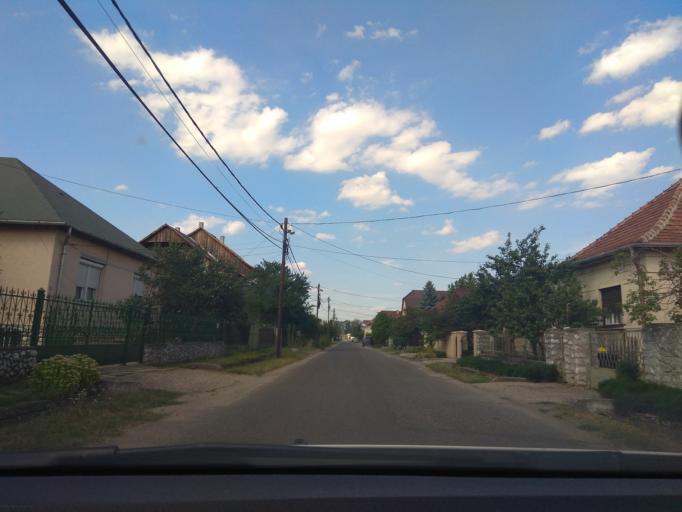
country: HU
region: Borsod-Abauj-Zemplen
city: Miskolc
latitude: 48.0550
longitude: 20.7936
